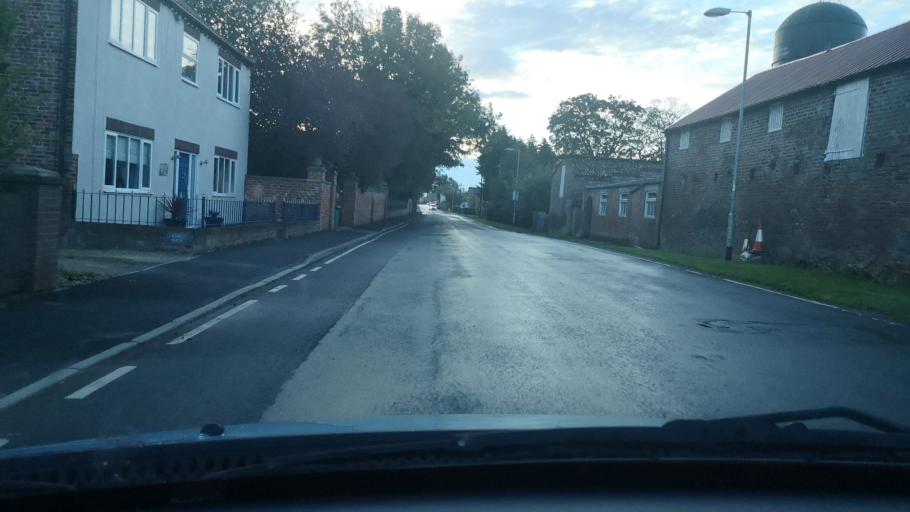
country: GB
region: England
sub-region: East Riding of Yorkshire
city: Laxton
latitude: 53.6994
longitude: -0.7989
